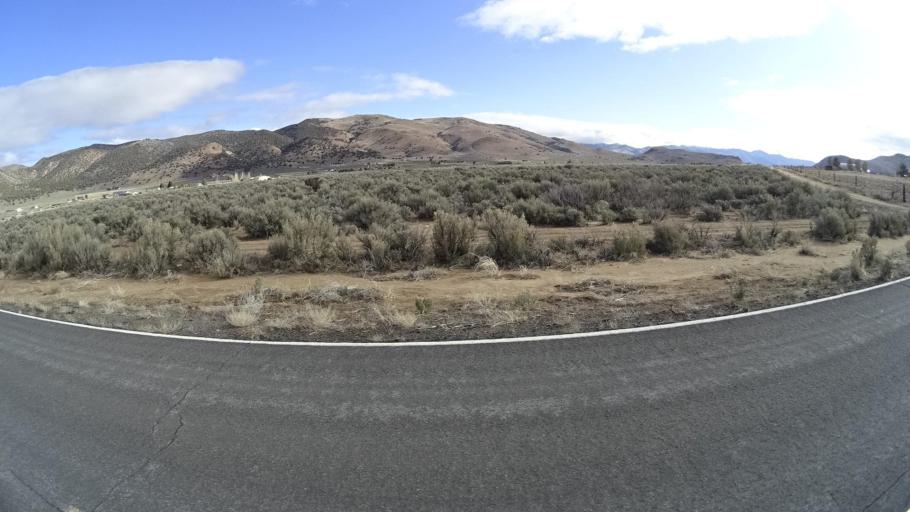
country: US
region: Nevada
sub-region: Washoe County
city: Cold Springs
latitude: 39.8908
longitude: -119.9790
